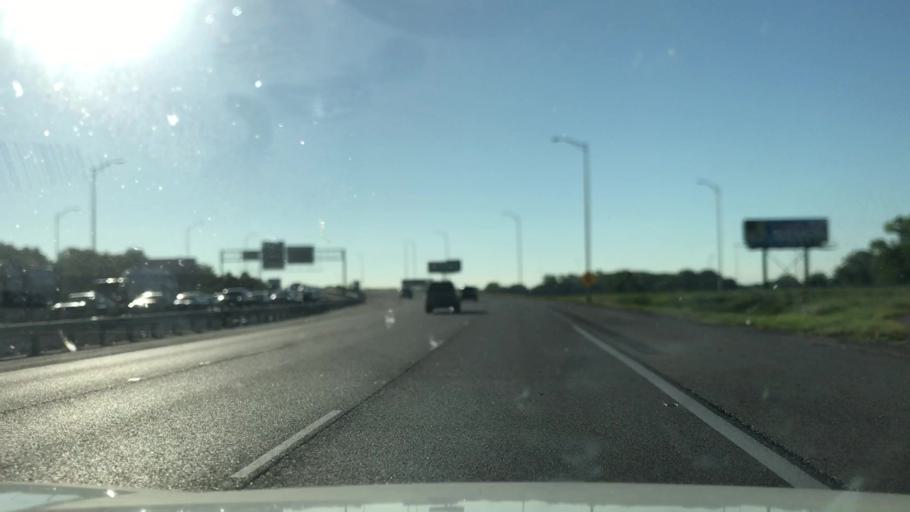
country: US
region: Illinois
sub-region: Saint Clair County
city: East Saint Louis
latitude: 38.6217
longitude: -90.1230
